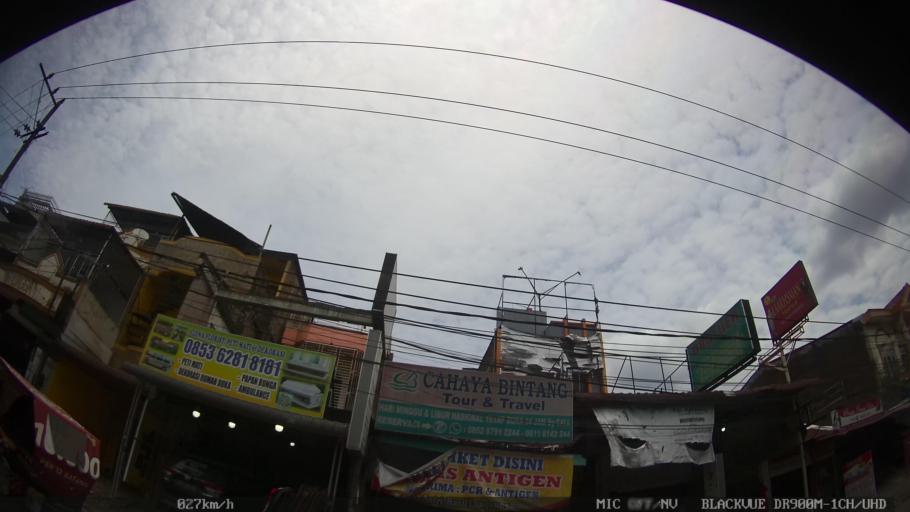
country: ID
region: North Sumatra
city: Deli Tua
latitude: 3.5381
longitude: 98.6519
